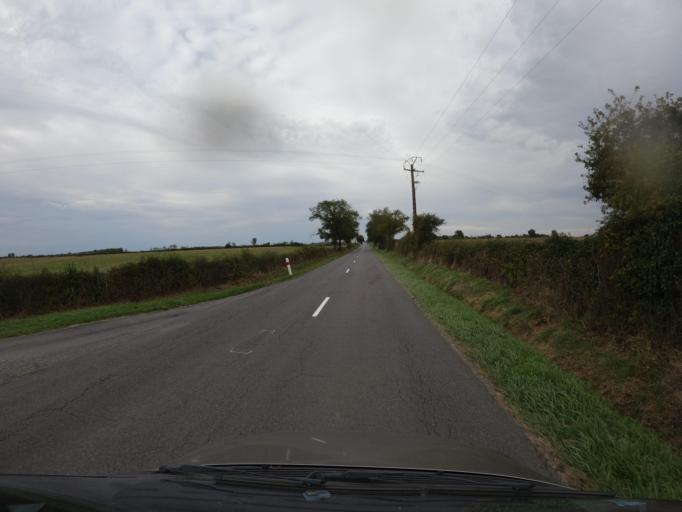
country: FR
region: Poitou-Charentes
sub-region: Departement de la Vienne
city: Saulge
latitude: 46.3725
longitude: 0.8428
